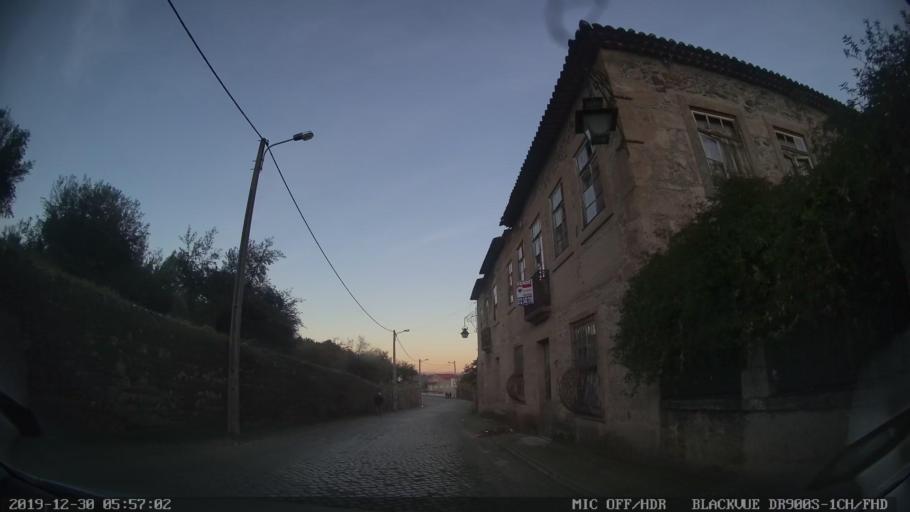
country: PT
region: Castelo Branco
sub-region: Idanha-A-Nova
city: Idanha-a-Nova
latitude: 40.0272
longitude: -7.2399
